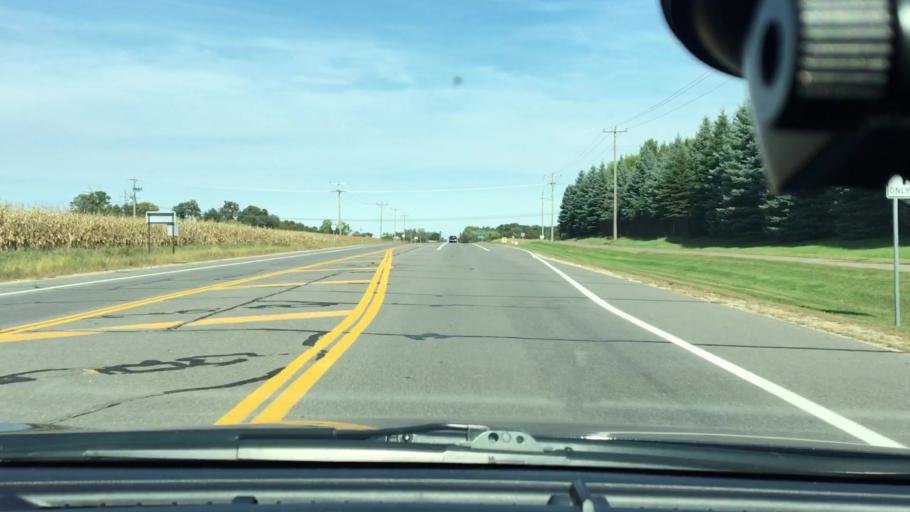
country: US
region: Minnesota
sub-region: Wright County
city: Hanover
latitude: 45.1726
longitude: -93.6657
